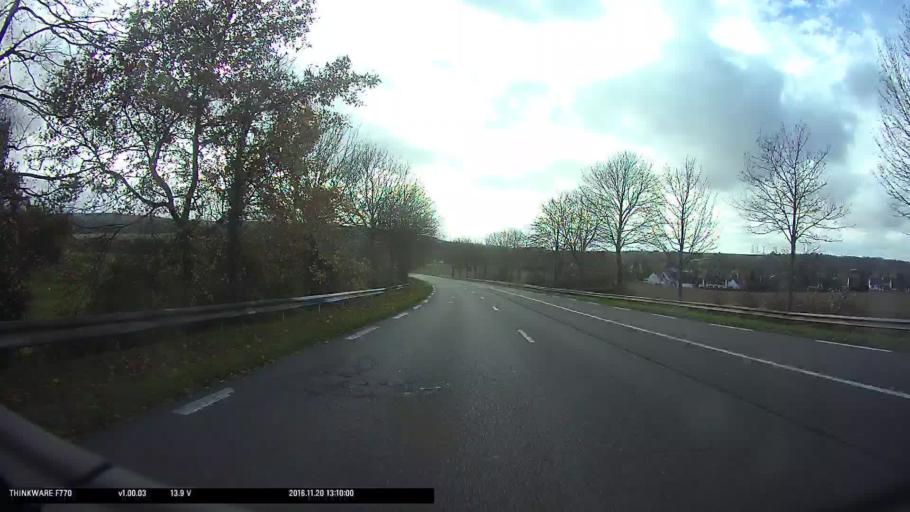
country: FR
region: Ile-de-France
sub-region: Departement du Val-d'Oise
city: Sagy
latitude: 49.0525
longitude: 1.9577
